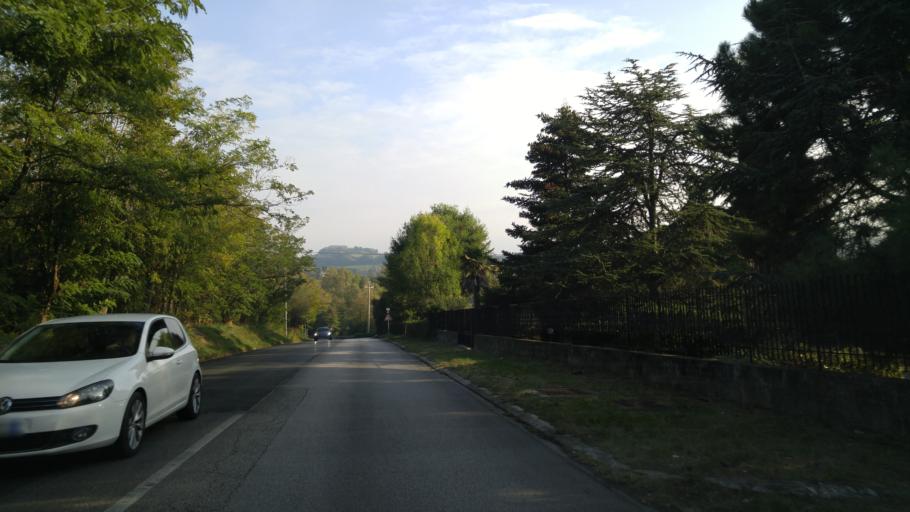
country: IT
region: The Marches
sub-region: Provincia di Pesaro e Urbino
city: Fenile
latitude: 43.8815
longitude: 12.9592
